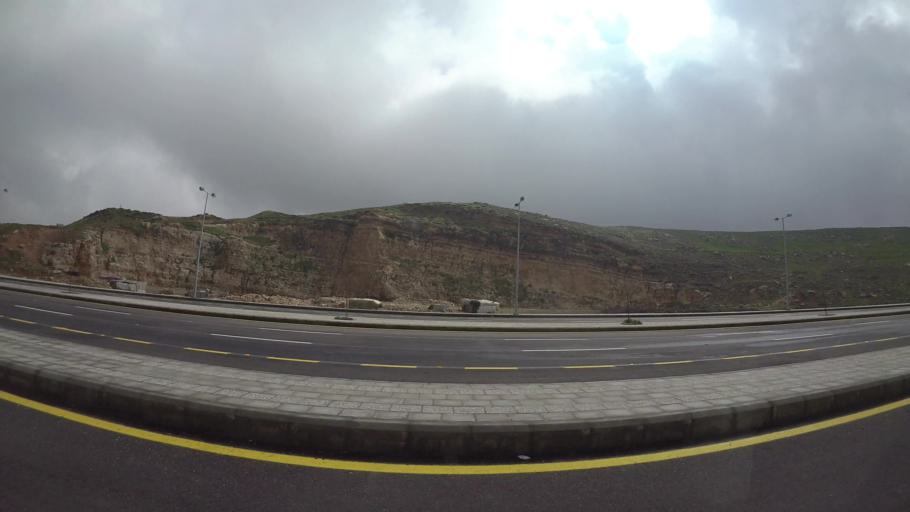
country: JO
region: Amman
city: Al Bunayyat ash Shamaliyah
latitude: 31.9340
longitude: 35.8708
